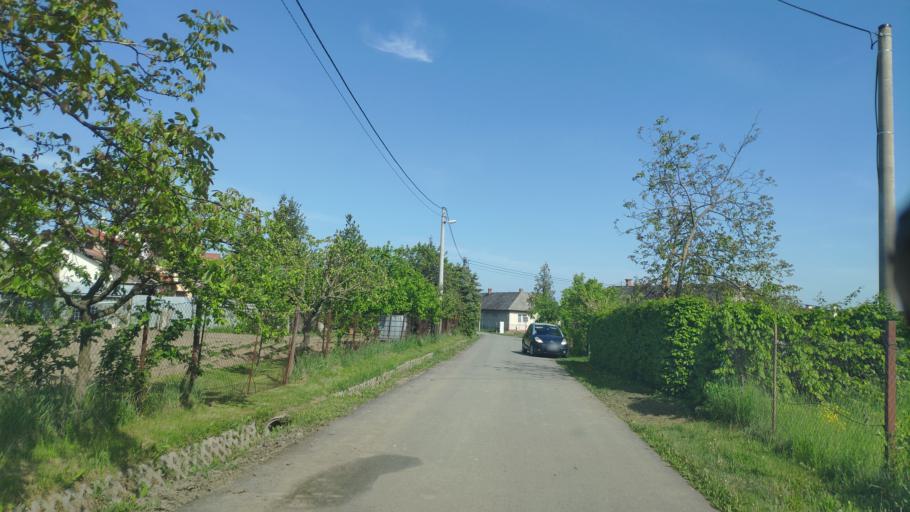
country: SK
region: Kosicky
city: Secovce
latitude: 48.6836
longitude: 21.6125
